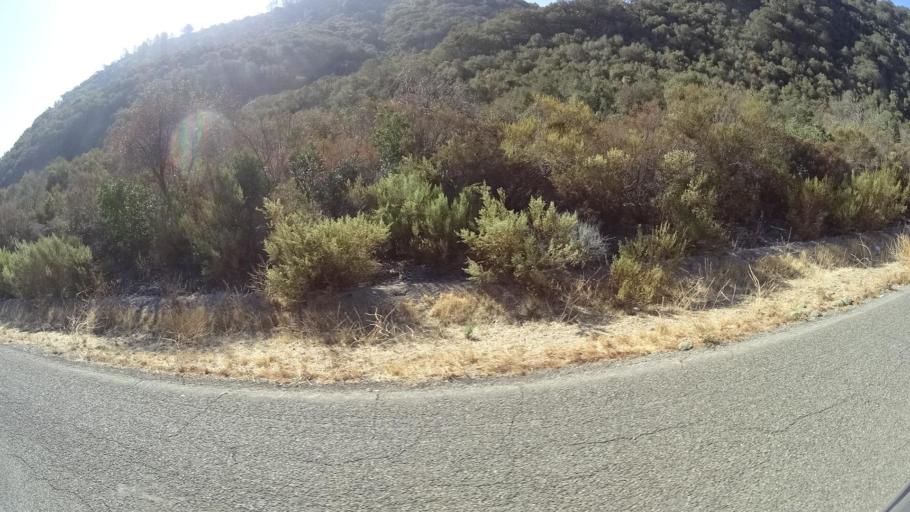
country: US
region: California
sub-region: Monterey County
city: King City
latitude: 36.0460
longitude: -121.0676
